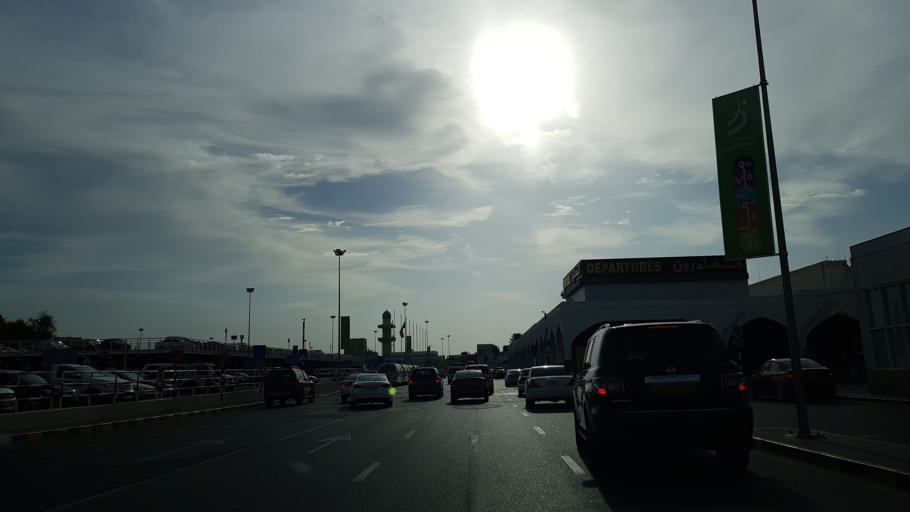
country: OM
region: Muhafazat Masqat
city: Bawshar
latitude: 23.5882
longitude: 58.2916
